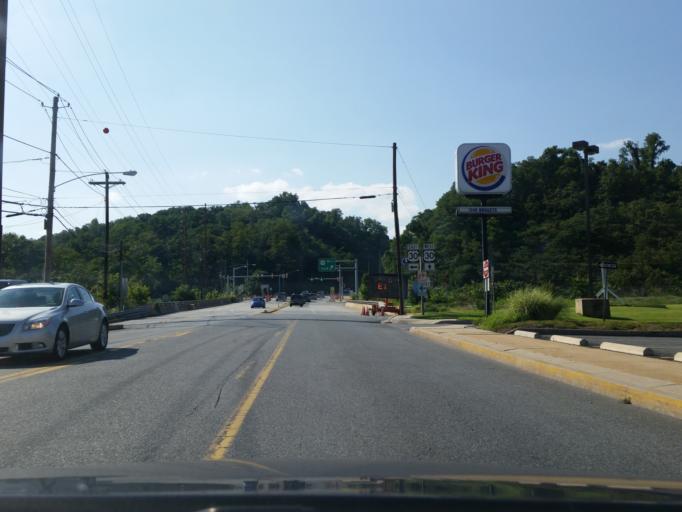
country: US
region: Pennsylvania
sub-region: Lancaster County
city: Columbia
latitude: 40.0377
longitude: -76.5090
